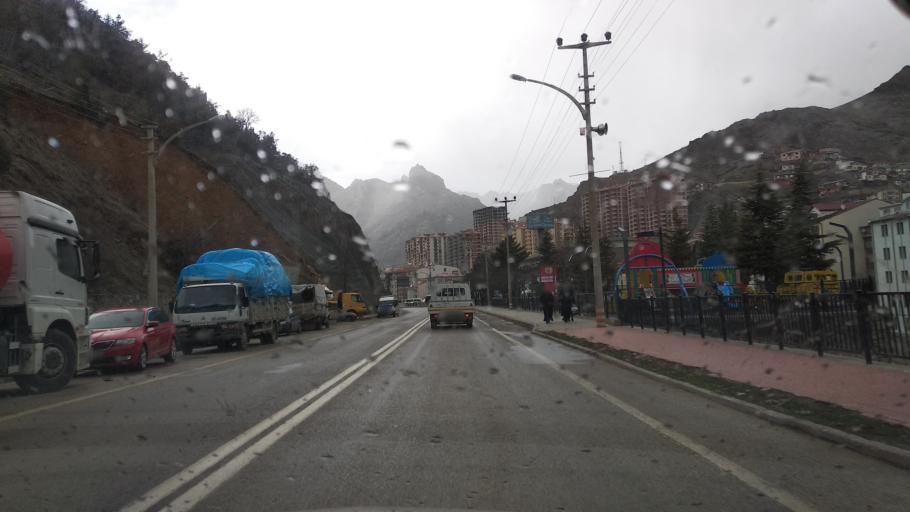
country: TR
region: Gumushane
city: Gumushkhane
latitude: 40.4594
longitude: 39.4749
